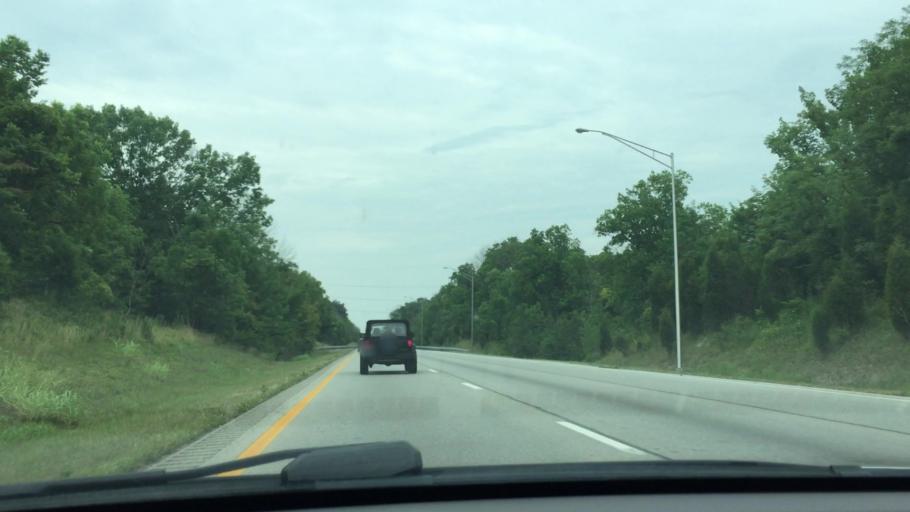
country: US
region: Kentucky
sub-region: Oldham County
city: Buckner
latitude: 38.3789
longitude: -85.4206
